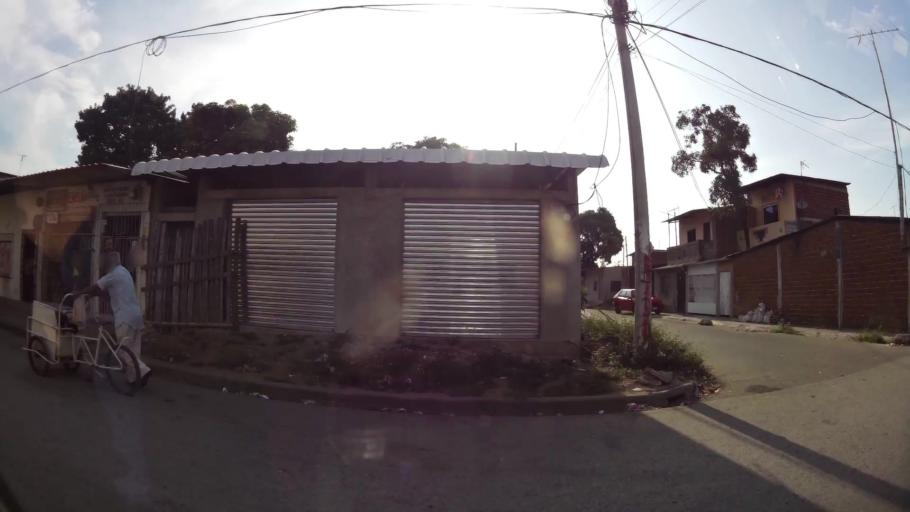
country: EC
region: Guayas
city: Eloy Alfaro
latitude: -2.0753
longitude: -79.9266
